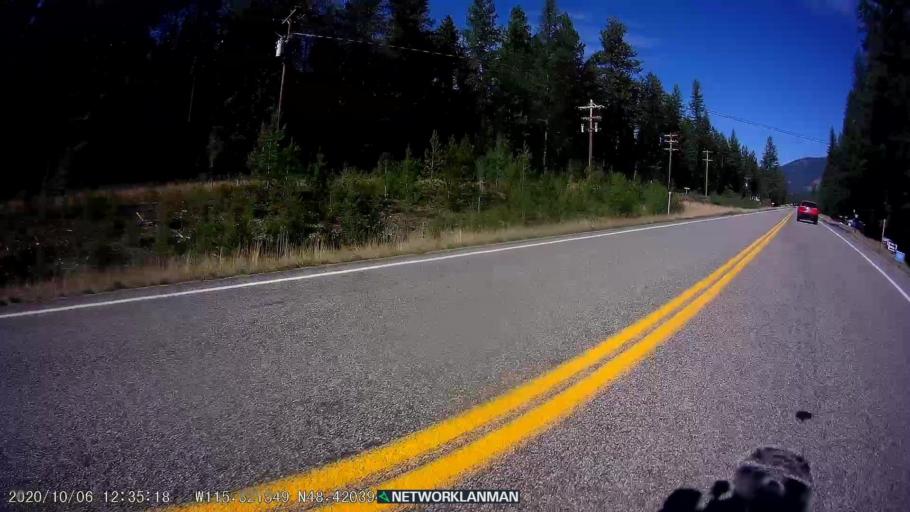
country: US
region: Montana
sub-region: Lincoln County
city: Libby
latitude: 48.4207
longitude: -115.8215
